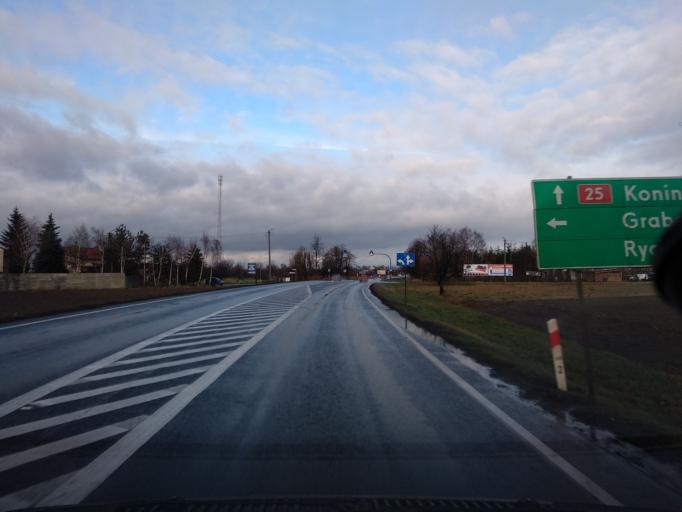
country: PL
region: Greater Poland Voivodeship
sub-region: Powiat koninski
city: Rychwal
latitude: 52.0721
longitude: 18.1580
